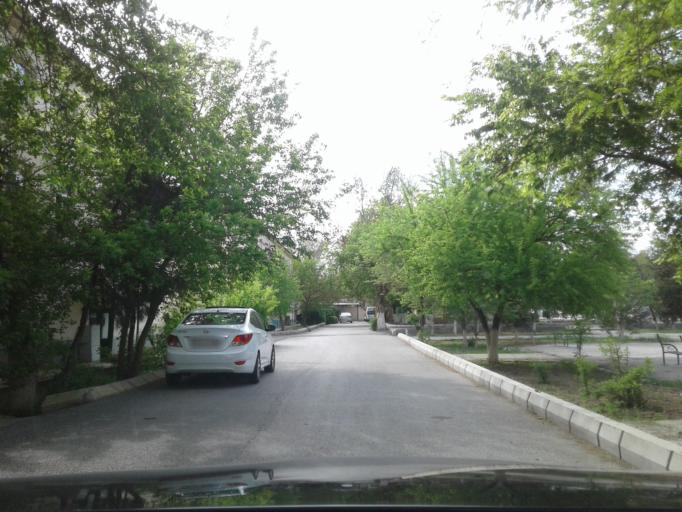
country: TM
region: Ahal
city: Ashgabat
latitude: 37.9574
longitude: 58.3562
